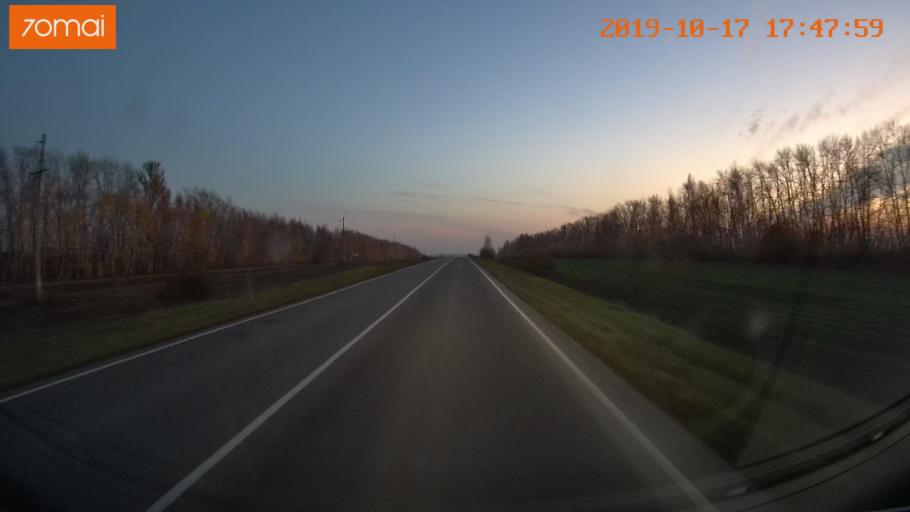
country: RU
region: Tula
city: Yepifan'
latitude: 53.6992
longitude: 38.6969
